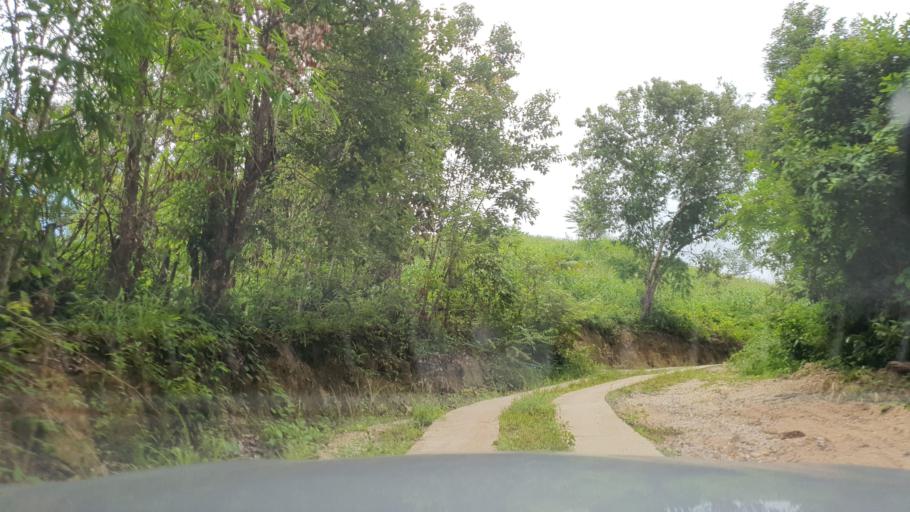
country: TH
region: Chiang Mai
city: Mae Wang
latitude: 18.6630
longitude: 98.6205
